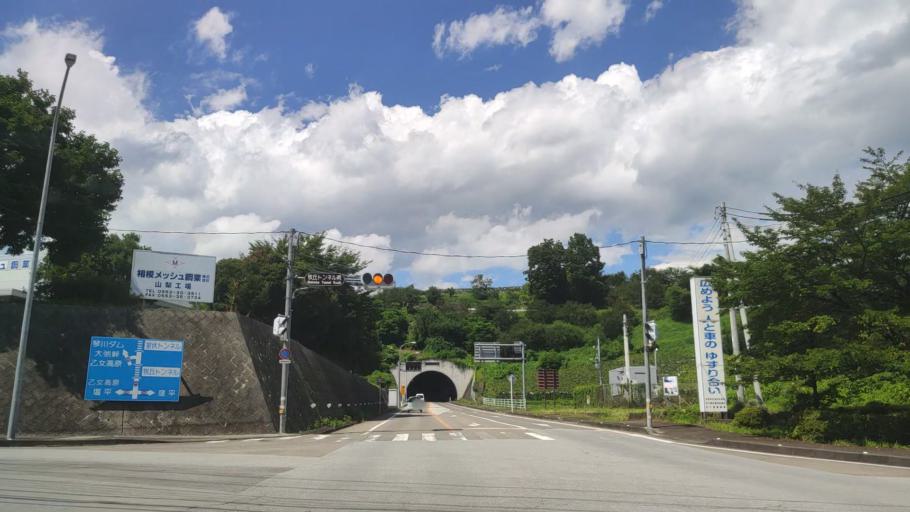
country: JP
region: Yamanashi
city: Enzan
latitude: 35.7422
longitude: 138.7077
